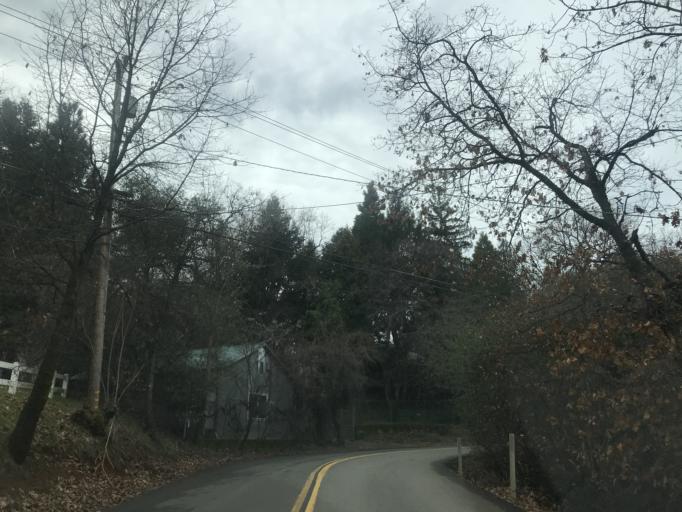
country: US
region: California
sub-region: El Dorado County
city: Placerville
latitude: 38.7278
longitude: -120.8206
